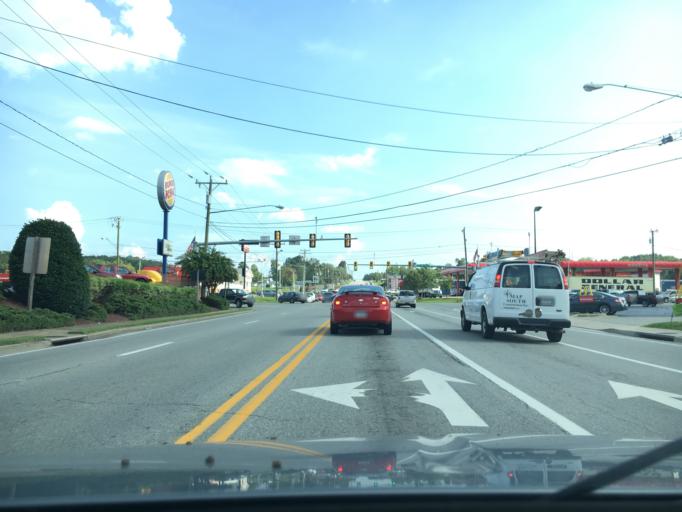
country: US
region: Virginia
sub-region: Halifax County
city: South Boston
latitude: 36.6882
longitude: -78.9002
